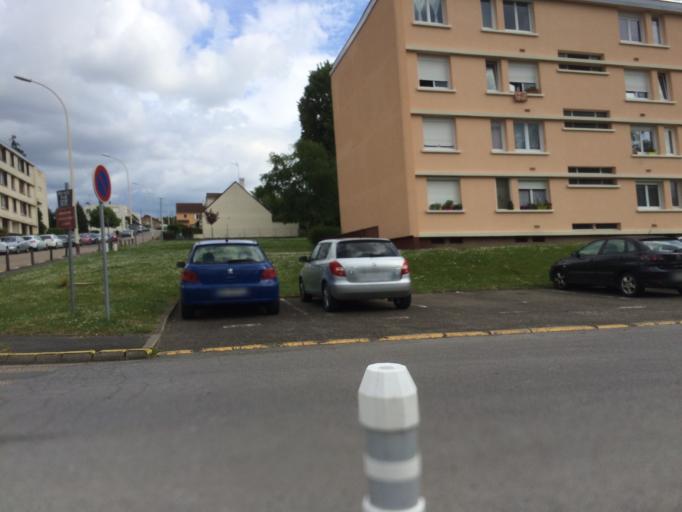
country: FR
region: Ile-de-France
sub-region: Departement de l'Essonne
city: Villiers-sur-Orge
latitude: 48.6518
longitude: 2.3045
